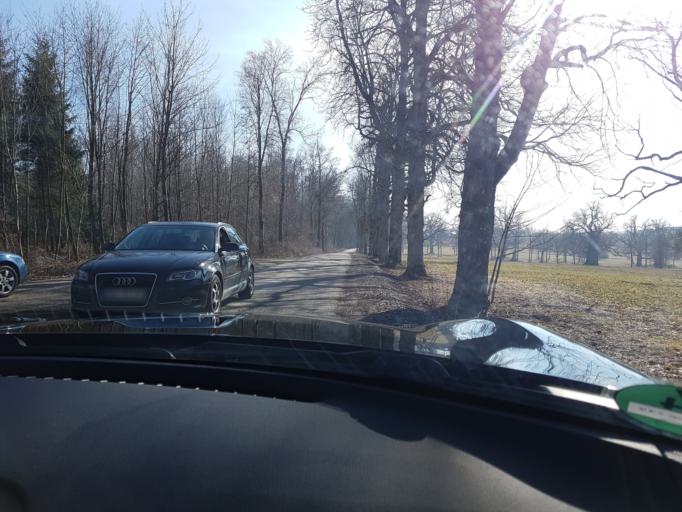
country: DE
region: Baden-Wuerttemberg
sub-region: Regierungsbezirk Stuttgart
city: Langenburg
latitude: 49.2730
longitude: 9.8870
